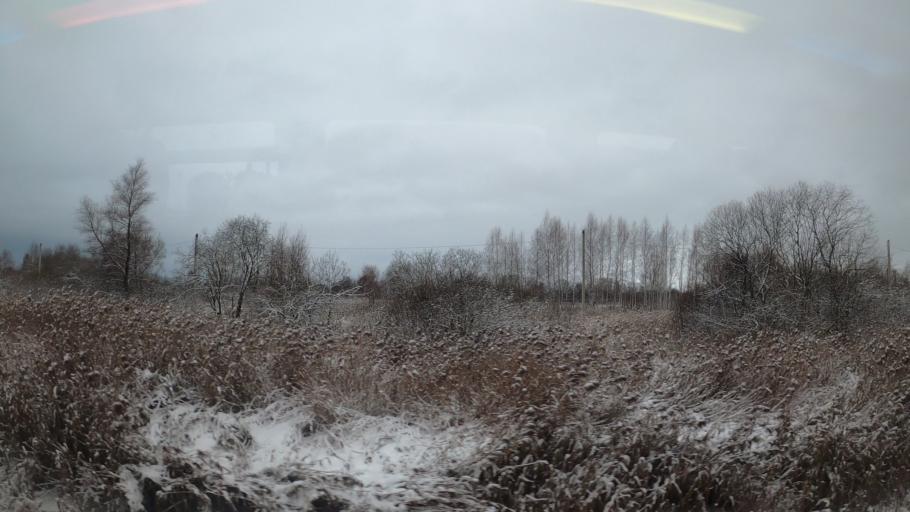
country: RU
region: Jaroslavl
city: Pereslavl'-Zalesskiy
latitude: 56.7263
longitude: 38.9038
